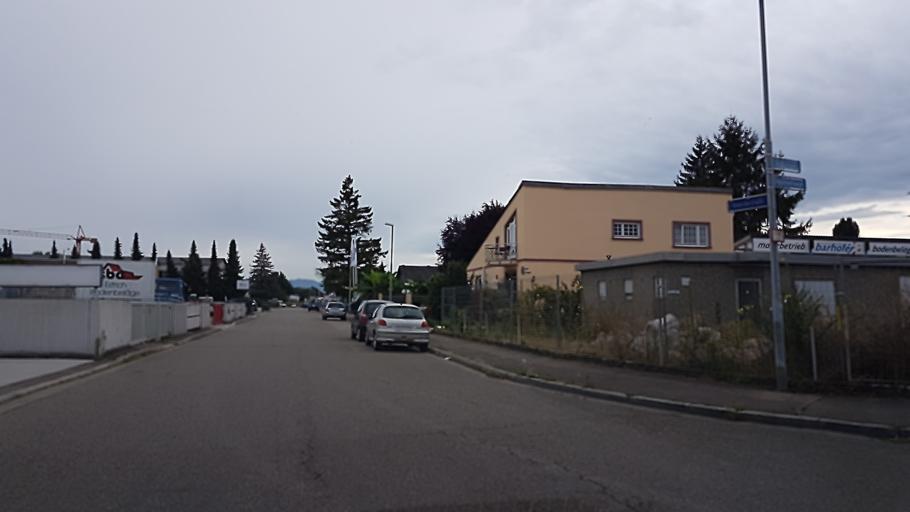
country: DE
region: Baden-Wuerttemberg
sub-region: Freiburg Region
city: Merdingen
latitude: 47.9979
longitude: 7.7189
